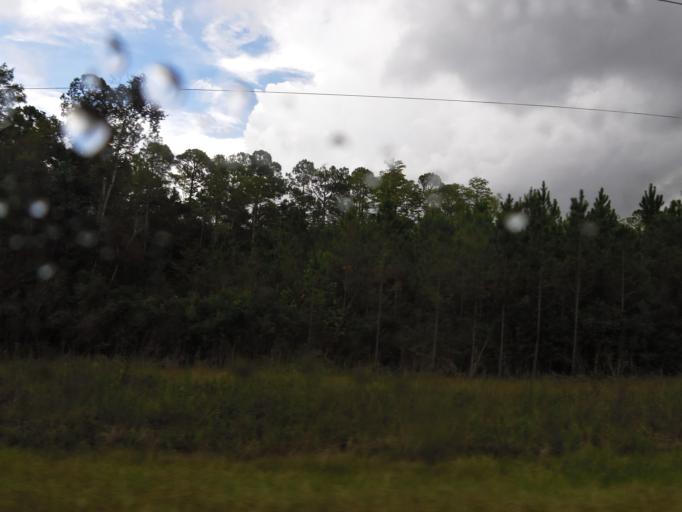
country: US
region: Florida
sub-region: Nassau County
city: Hilliard
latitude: 30.5696
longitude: -82.0444
